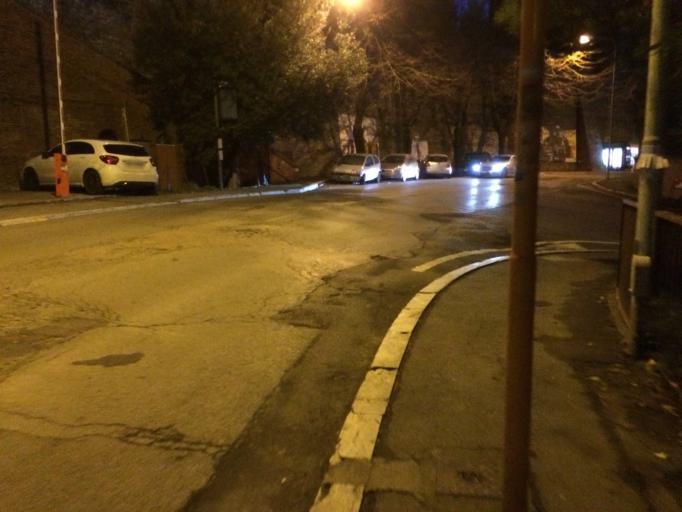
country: IT
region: Umbria
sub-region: Provincia di Perugia
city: Perugia
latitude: 43.1132
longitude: 12.3821
